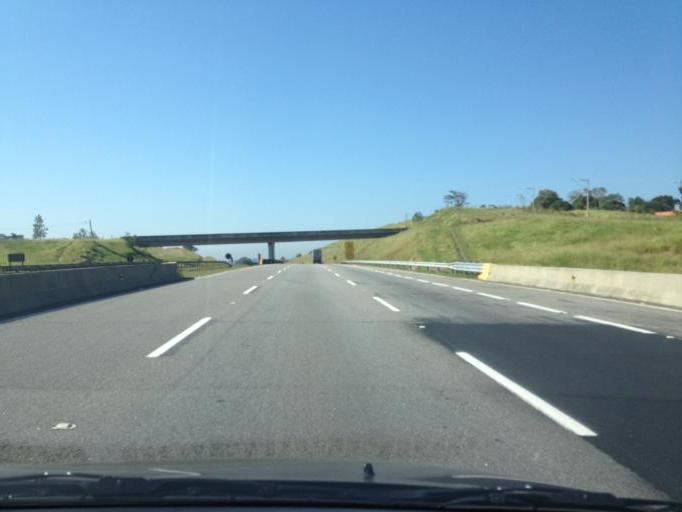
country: BR
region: Sao Paulo
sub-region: Guararema
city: Guararema
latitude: -23.3597
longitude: -46.1018
